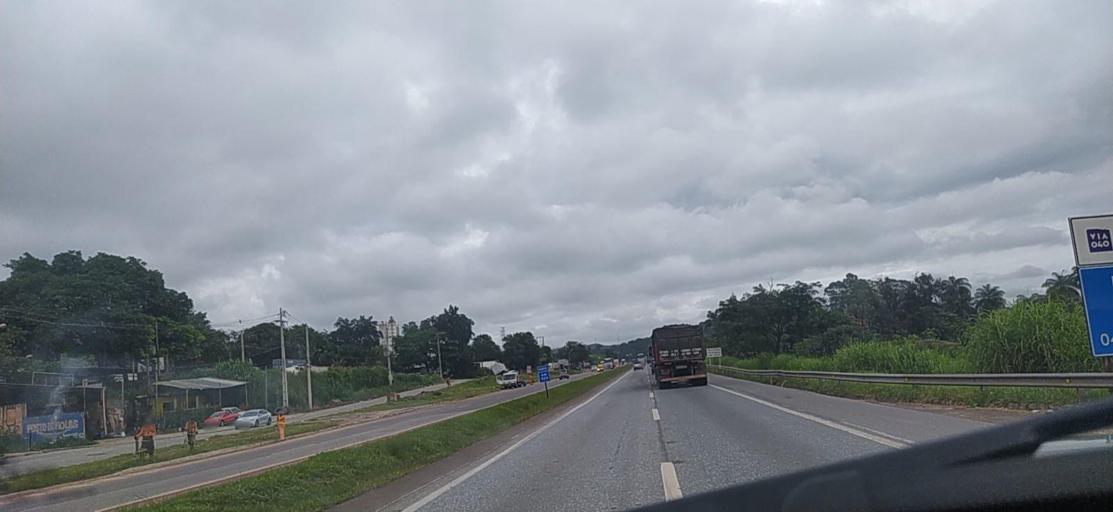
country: BR
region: Minas Gerais
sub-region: Contagem
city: Contagem
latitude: -19.8761
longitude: -44.0530
